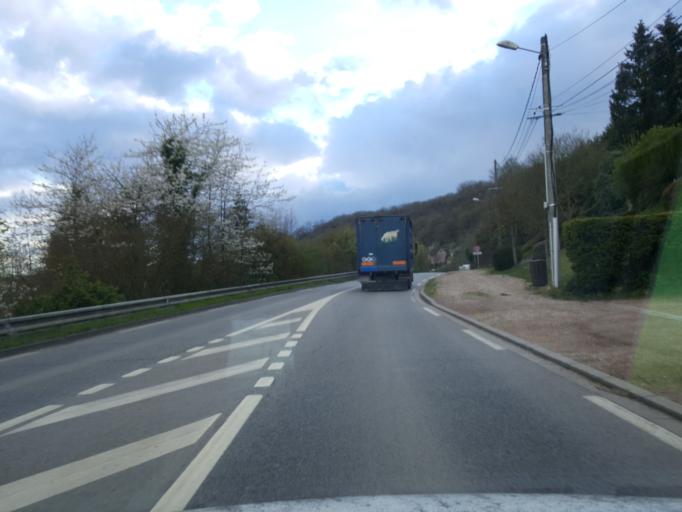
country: FR
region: Ile-de-France
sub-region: Departement des Yvelines
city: Mantes-la-Ville
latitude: 48.9528
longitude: 1.7040
